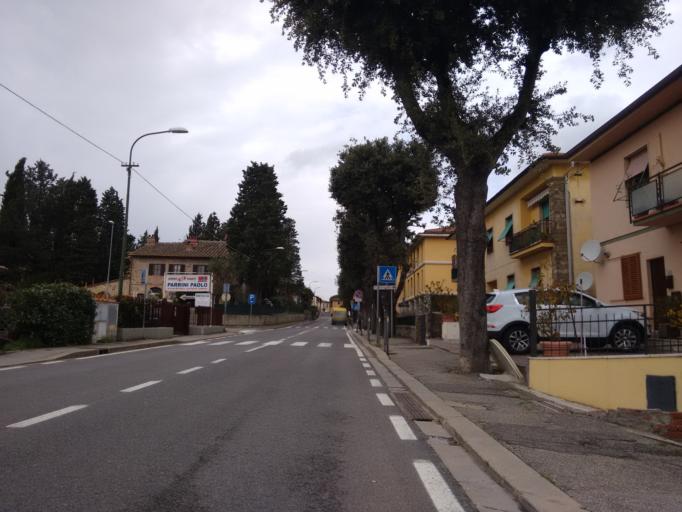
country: IT
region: Tuscany
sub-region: Province of Florence
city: Strada in Chianti
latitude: 43.6572
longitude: 11.3006
